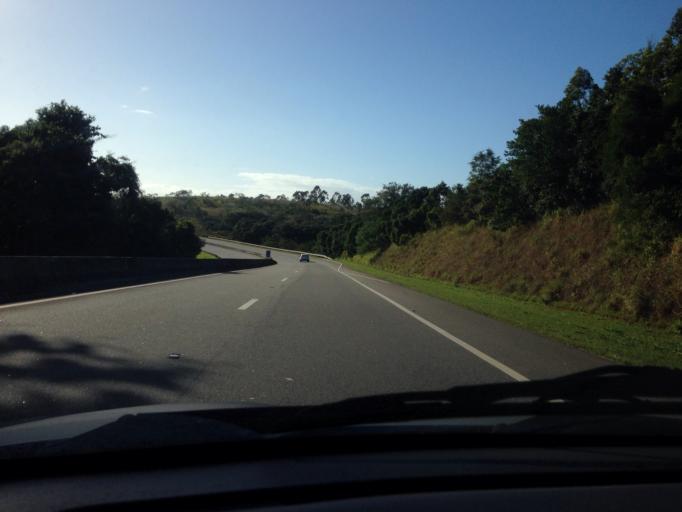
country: BR
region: Espirito Santo
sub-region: Guarapari
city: Guarapari
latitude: -20.6270
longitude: -40.5038
